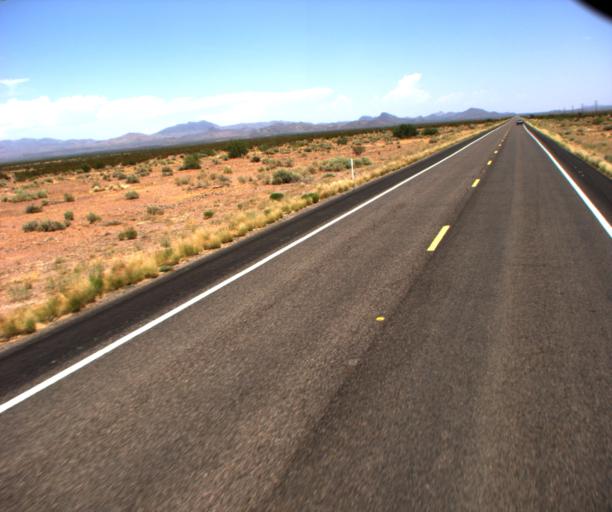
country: US
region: Arizona
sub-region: Graham County
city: Safford
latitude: 32.7814
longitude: -109.5321
